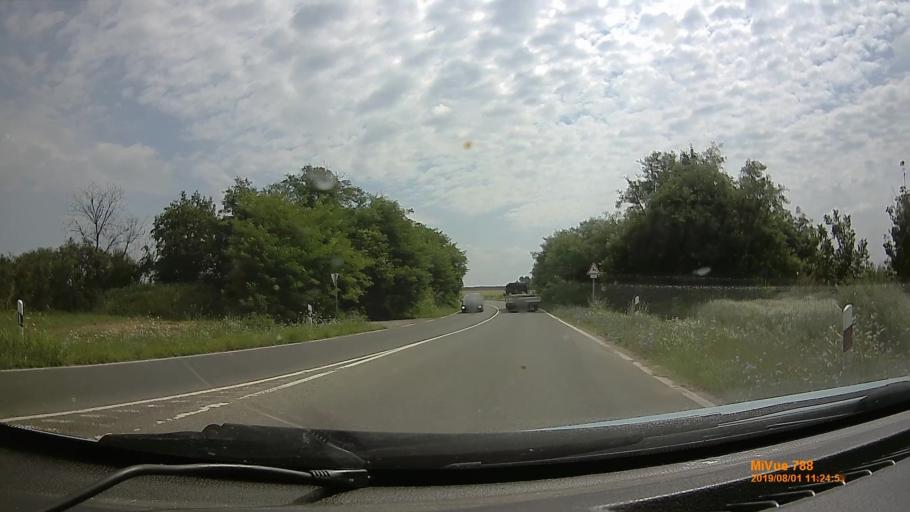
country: HU
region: Baranya
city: Kozarmisleny
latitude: 46.0153
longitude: 18.2894
